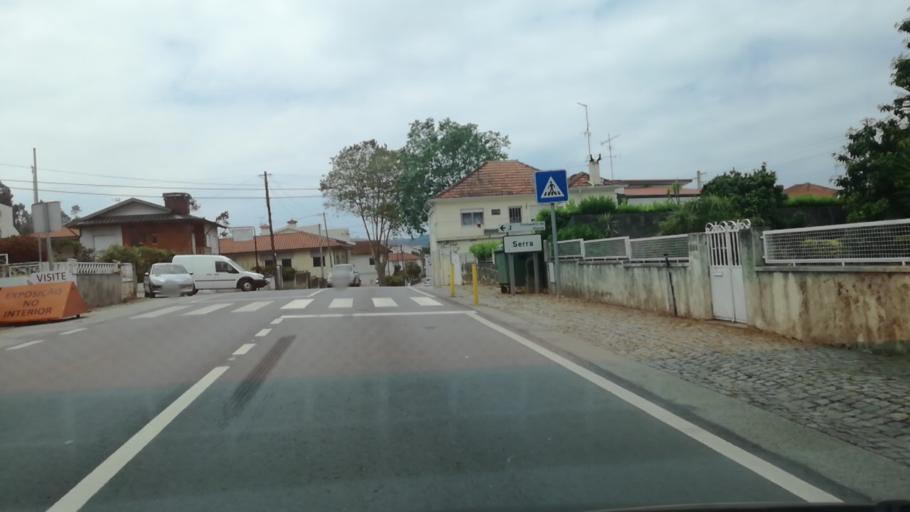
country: PT
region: Porto
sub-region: Trofa
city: Sao Romao do Coronado
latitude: 41.3047
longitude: -8.5885
